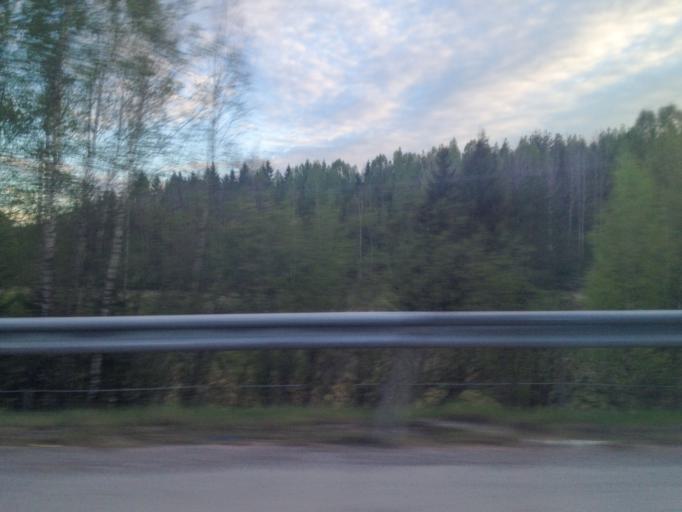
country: FI
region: Uusimaa
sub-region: Helsinki
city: Hyvinge
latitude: 60.6502
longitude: 24.8031
